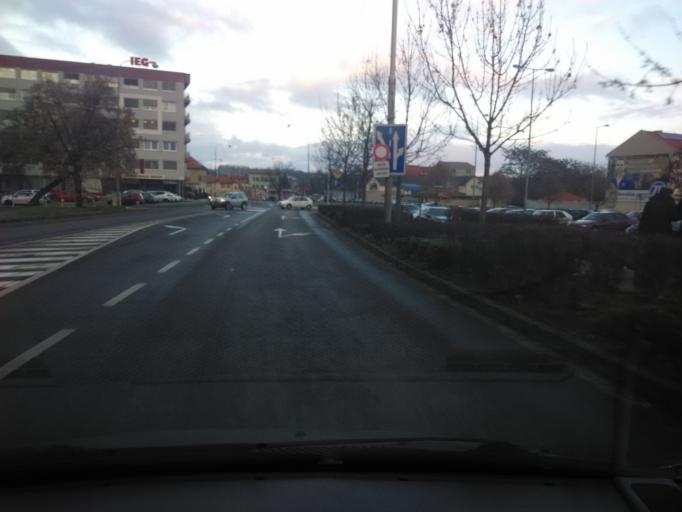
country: SK
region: Nitriansky
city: Levice
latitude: 48.2160
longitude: 18.6069
